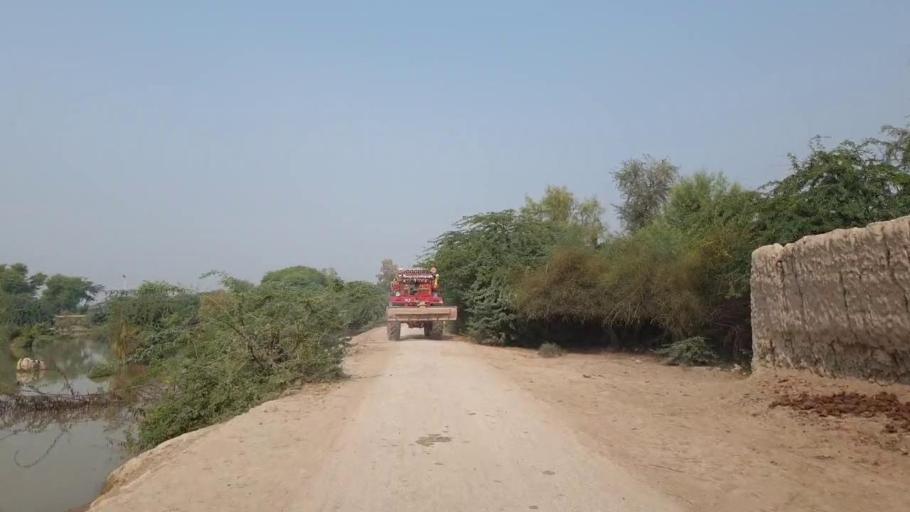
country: PK
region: Sindh
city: Bhan
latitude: 26.5406
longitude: 67.7012
